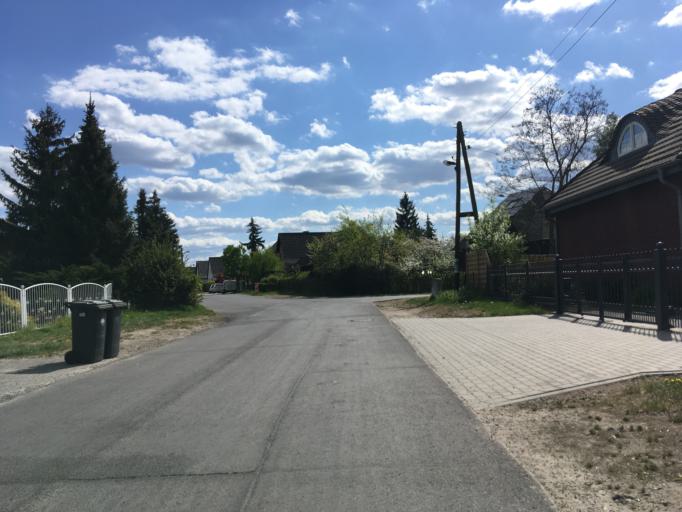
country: DE
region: Berlin
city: Hellersdorf
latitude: 52.5313
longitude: 13.6308
